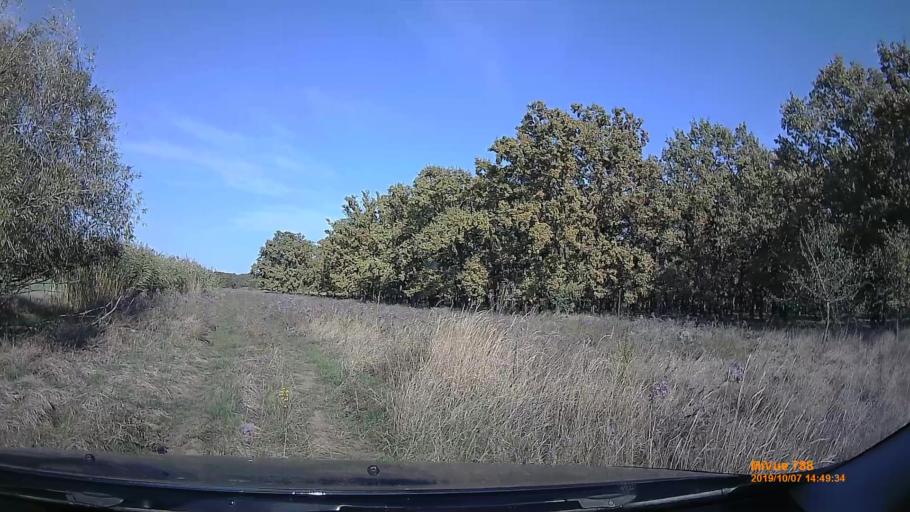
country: HU
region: Jasz-Nagykun-Szolnok
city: Kunszentmarton
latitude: 46.8593
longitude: 20.3239
